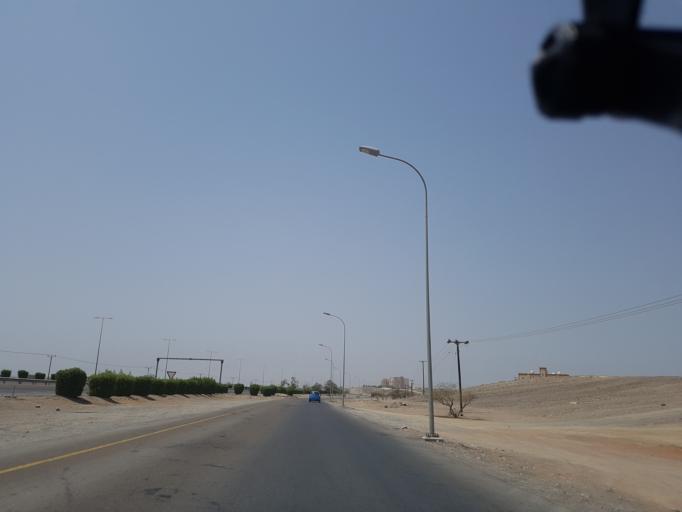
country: OM
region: Al Batinah
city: Al Liwa'
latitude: 24.4138
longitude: 56.5995
